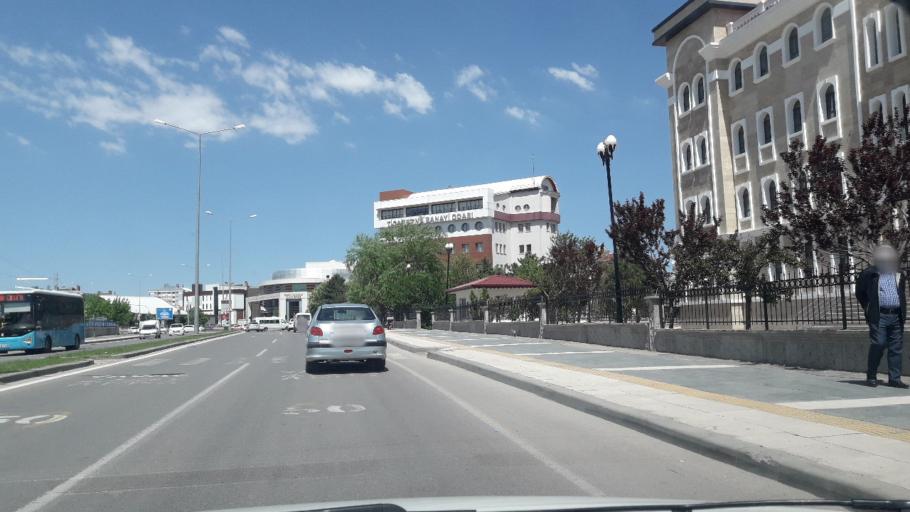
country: TR
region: Sivas
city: Sivas
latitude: 39.7411
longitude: 37.0142
